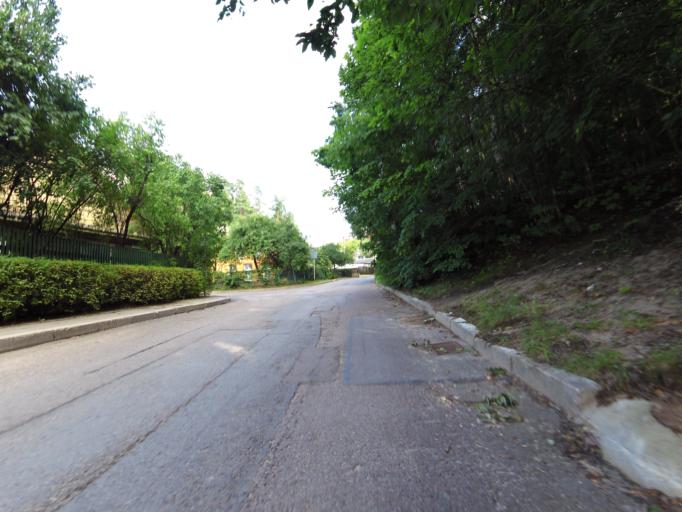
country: LT
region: Vilnius County
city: Rasos
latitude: 54.6966
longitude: 25.3167
